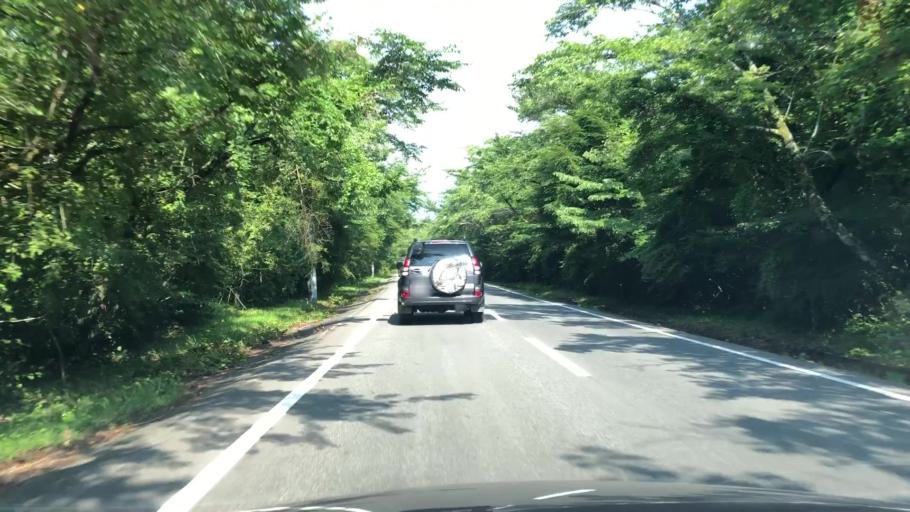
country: JP
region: Shizuoka
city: Gotemba
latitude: 35.3278
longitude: 138.8496
